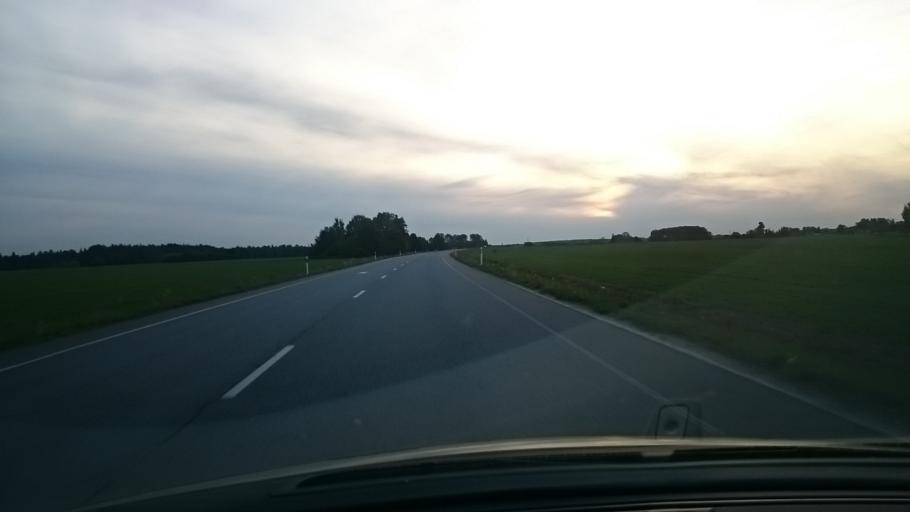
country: EE
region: Jaervamaa
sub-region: Tueri vald
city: Sarevere
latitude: 58.7672
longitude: 25.5308
